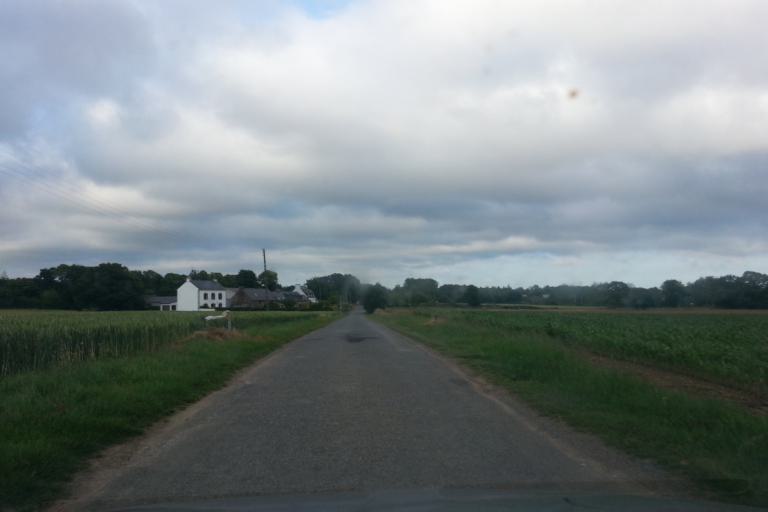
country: FR
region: Brittany
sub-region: Departement du Finistere
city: Mellac
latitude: 47.8854
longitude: -3.5937
